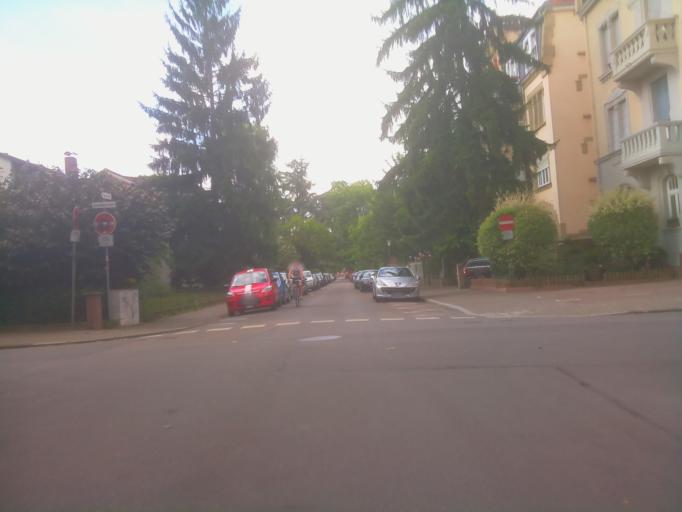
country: DE
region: Baden-Wuerttemberg
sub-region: Karlsruhe Region
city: Heidelberg
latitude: 49.4154
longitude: 8.6879
